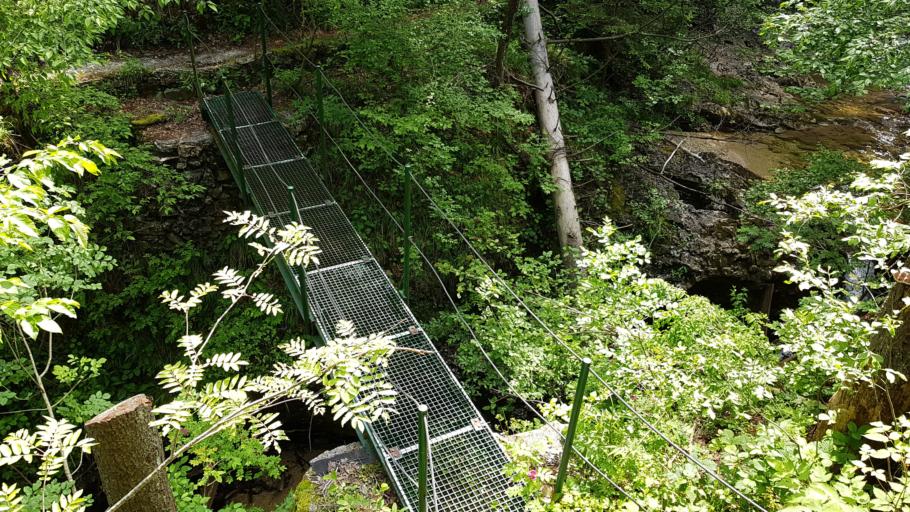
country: SI
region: Borovnica
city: Borovnica
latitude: 45.8815
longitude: 14.3701
